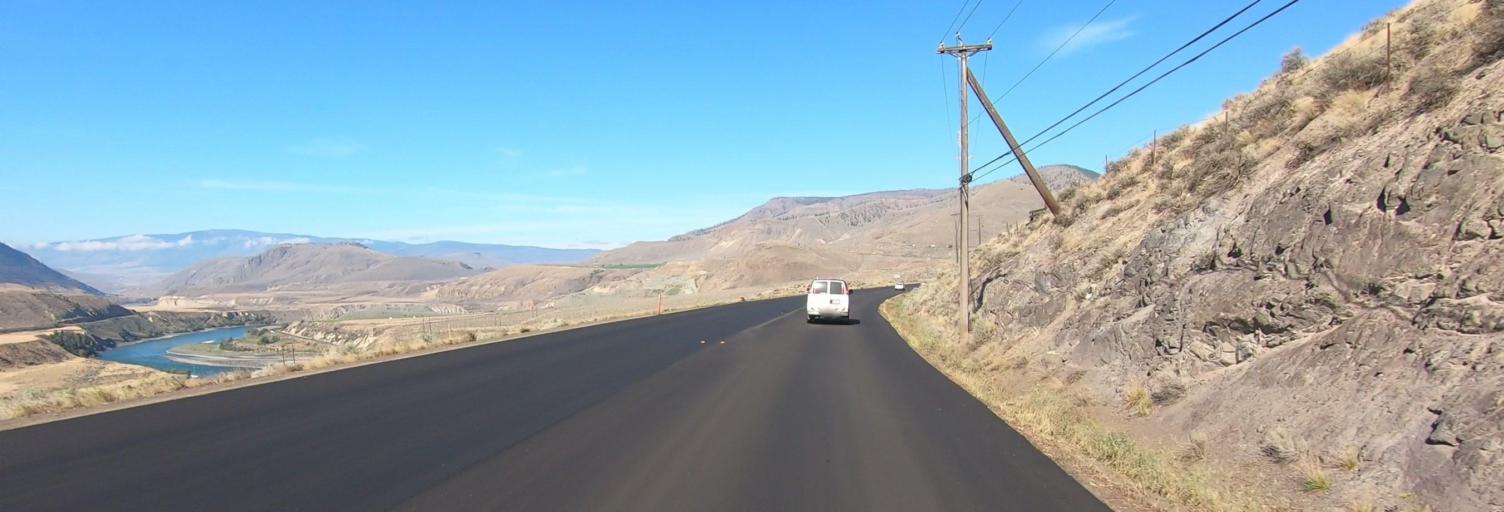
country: CA
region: British Columbia
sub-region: Thompson-Nicola Regional District
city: Ashcroft
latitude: 50.7912
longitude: -121.0833
